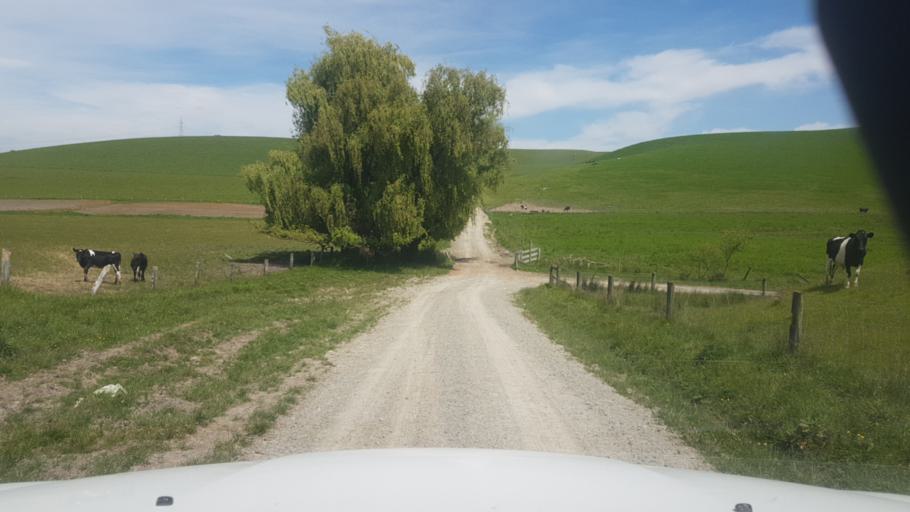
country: NZ
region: Canterbury
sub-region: Timaru District
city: Pleasant Point
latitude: -44.1285
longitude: 171.0104
